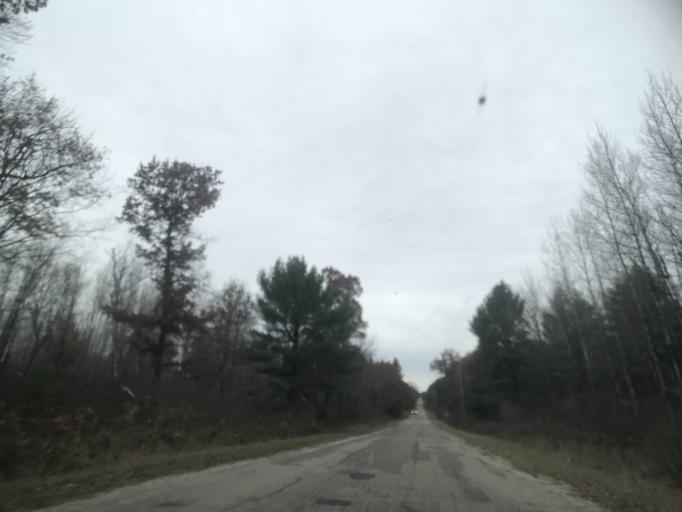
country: US
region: Wisconsin
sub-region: Oconto County
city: Gillett
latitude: 45.2872
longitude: -88.2570
